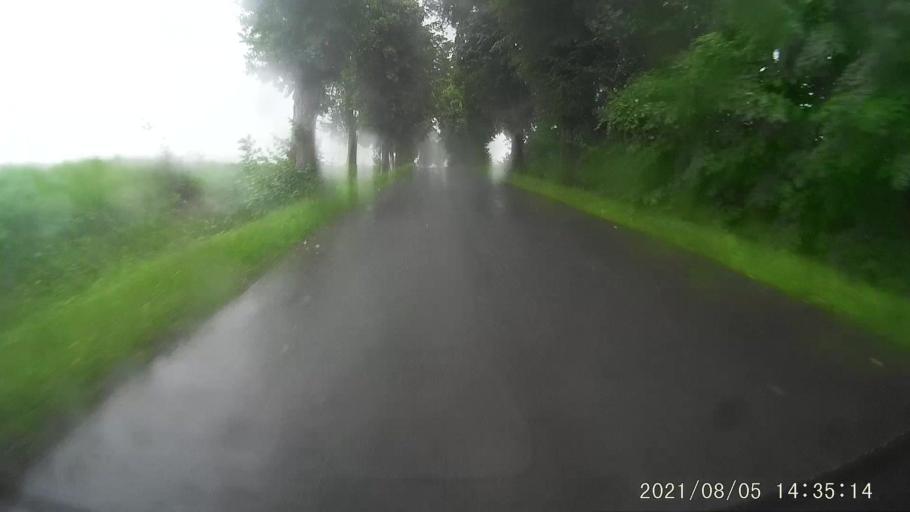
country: PL
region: Opole Voivodeship
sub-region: Powiat nyski
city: Lambinowice
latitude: 50.4673
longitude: 17.5054
